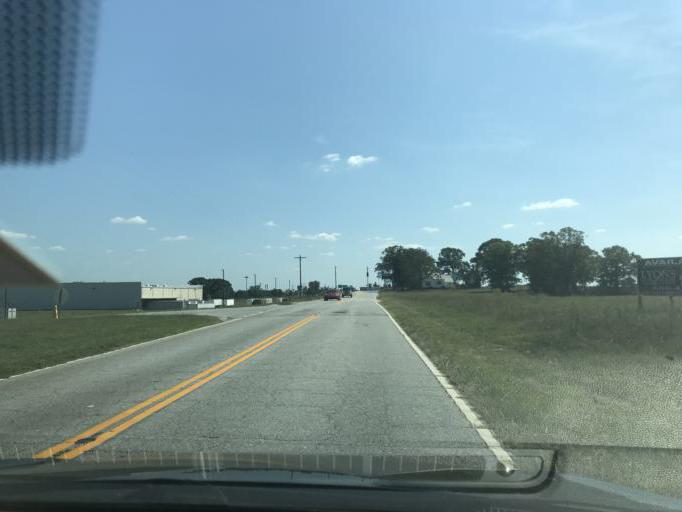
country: US
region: South Carolina
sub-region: Cherokee County
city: Gaffney
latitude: 35.0887
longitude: -81.7101
